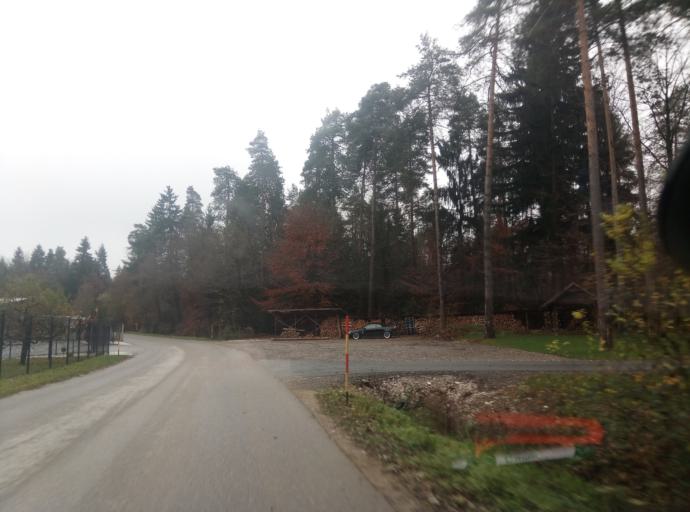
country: SI
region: Vodice
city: Vodice
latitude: 46.1681
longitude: 14.4822
